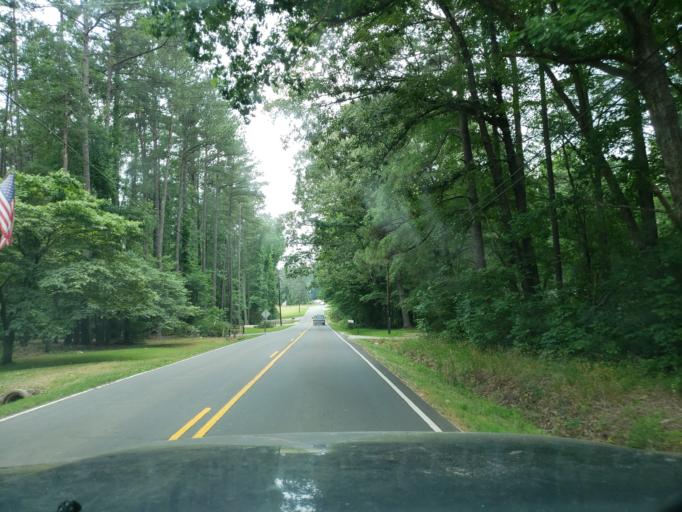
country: US
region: North Carolina
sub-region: Granville County
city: Butner
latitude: 36.1593
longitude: -78.8890
